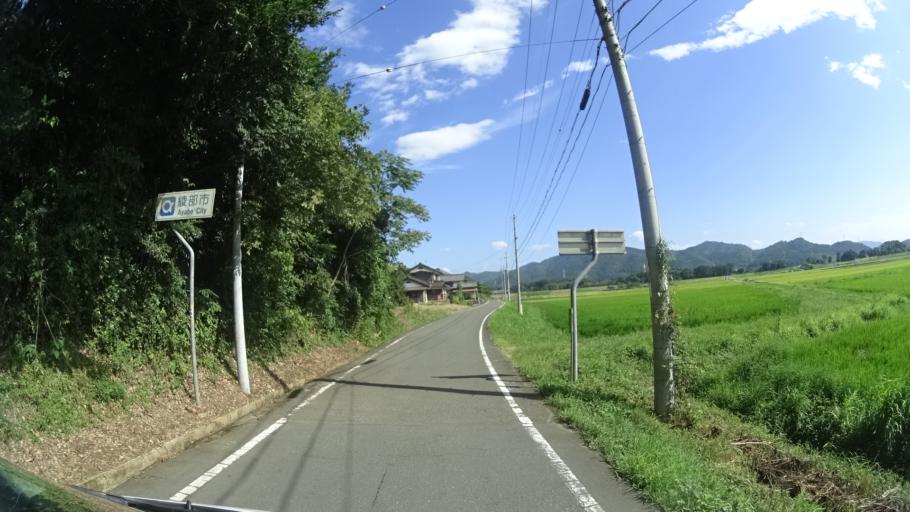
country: JP
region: Kyoto
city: Ayabe
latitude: 35.3166
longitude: 135.1885
